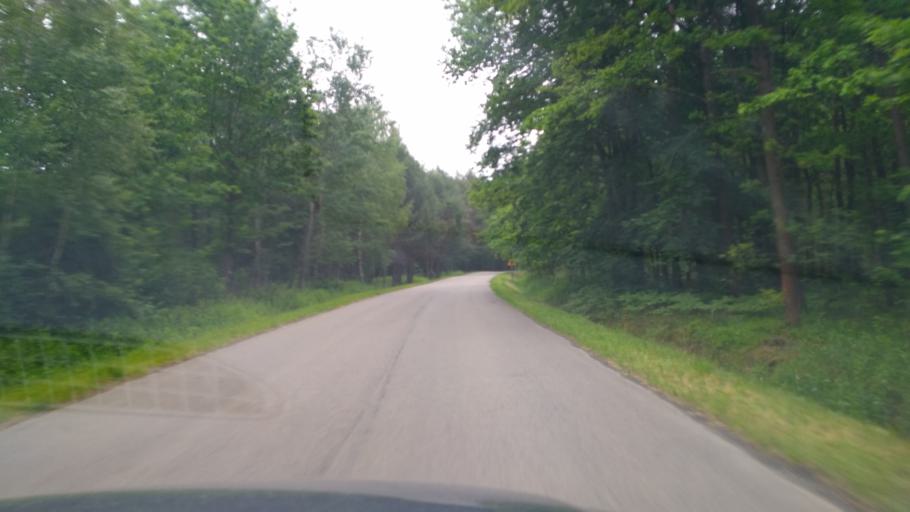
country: PL
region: Subcarpathian Voivodeship
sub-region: Powiat kolbuszowski
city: Niwiska
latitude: 50.2123
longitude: 21.6612
